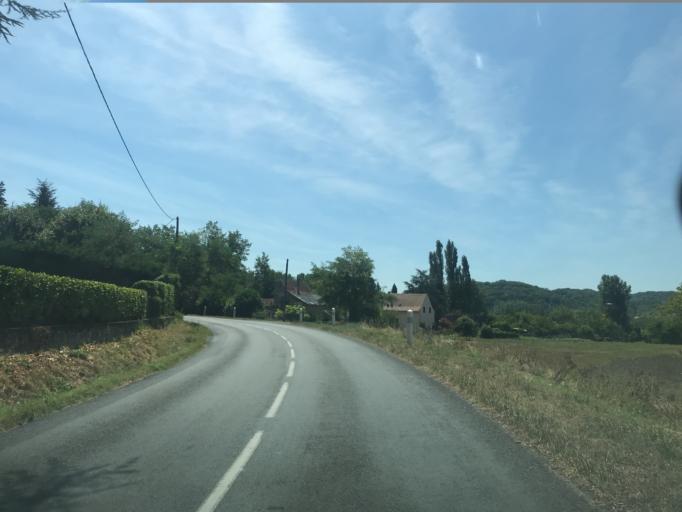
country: FR
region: Aquitaine
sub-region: Departement de la Dordogne
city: Cenac-et-Saint-Julien
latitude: 44.8100
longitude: 1.1973
